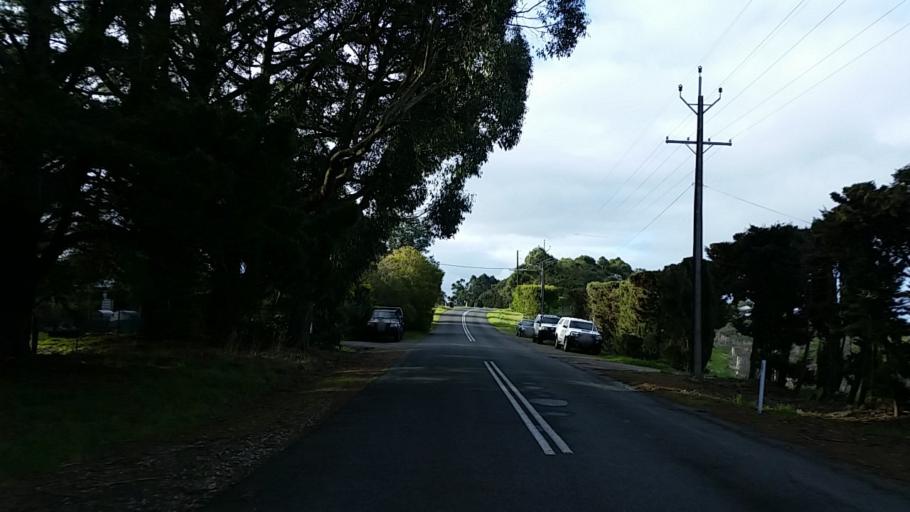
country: AU
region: South Australia
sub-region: Adelaide Hills
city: Bridgewater
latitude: -34.9613
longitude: 138.7508
